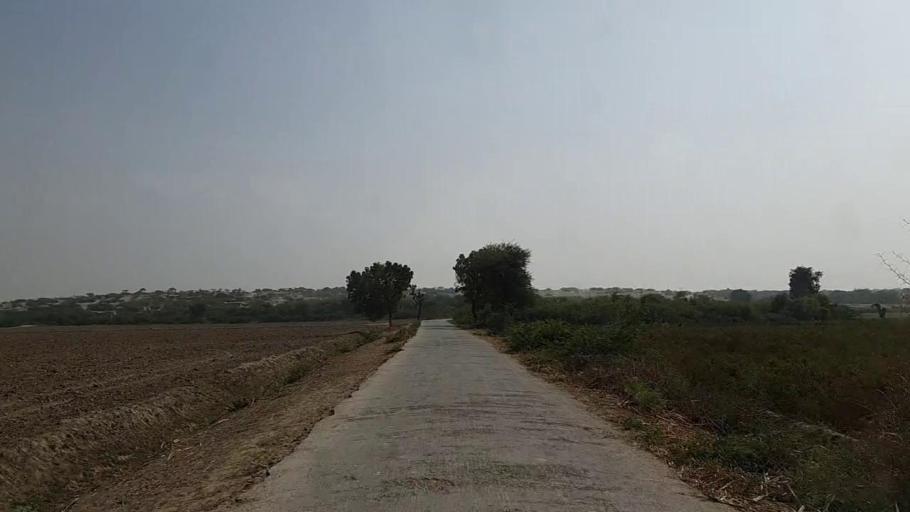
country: PK
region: Sindh
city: Naukot
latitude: 24.7488
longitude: 69.3472
